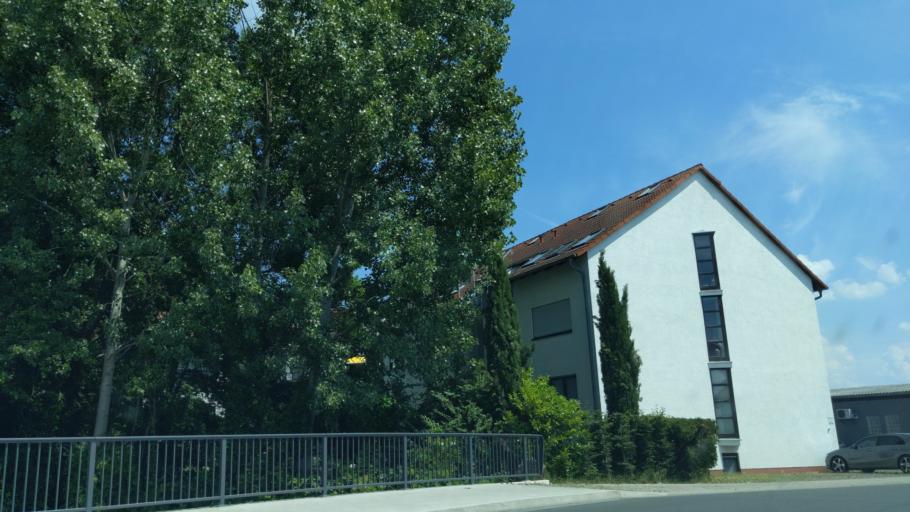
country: DE
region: Hesse
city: Dieburg
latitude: 49.8964
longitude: 8.8300
